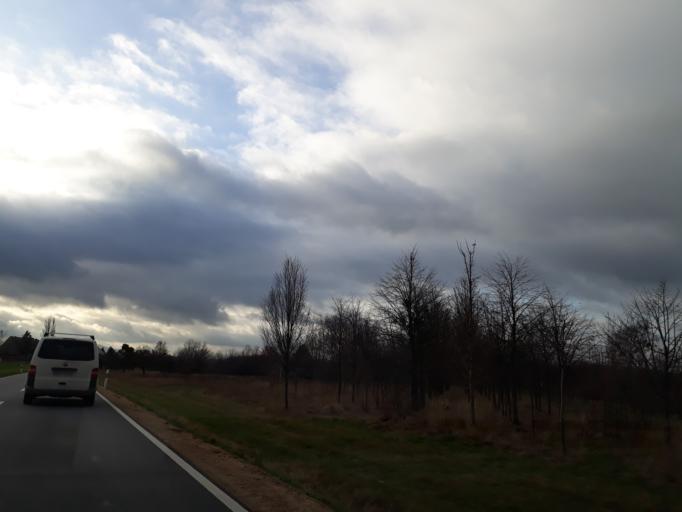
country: DE
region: Saxony
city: Weissenberg
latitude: 51.1903
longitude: 14.6457
